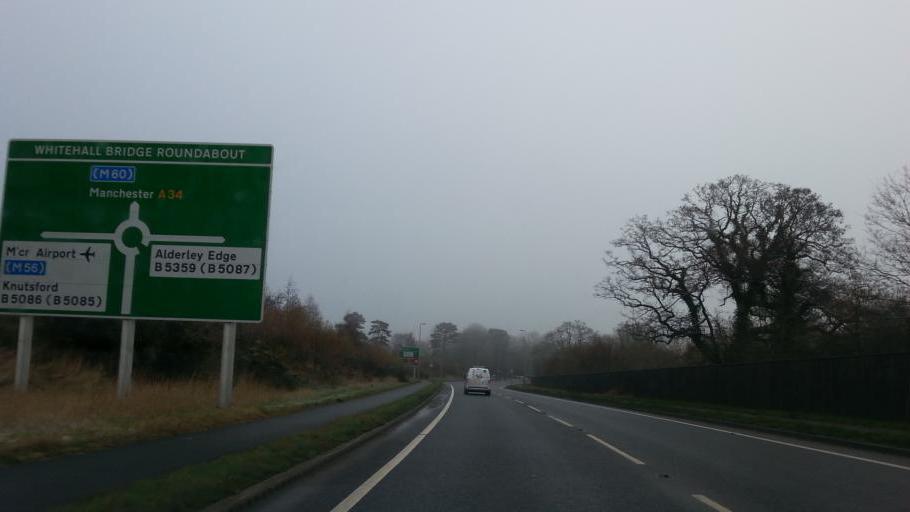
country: GB
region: England
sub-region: Cheshire East
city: Alderley Edge
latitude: 53.3108
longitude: -2.2392
